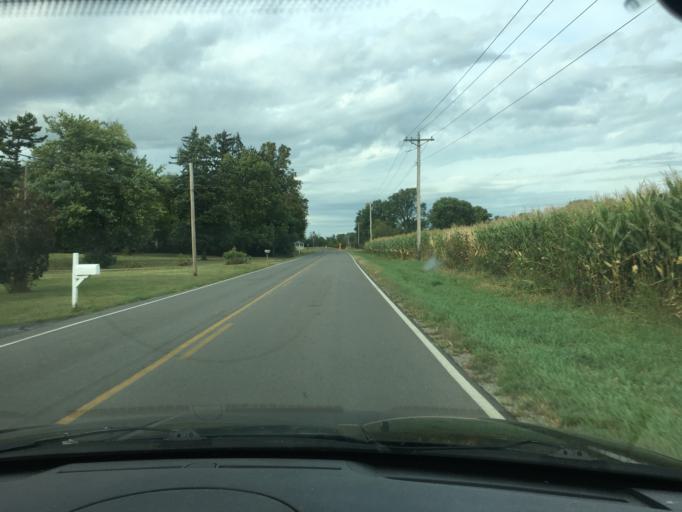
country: US
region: Ohio
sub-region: Logan County
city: Bellefontaine
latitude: 40.3178
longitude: -83.7953
